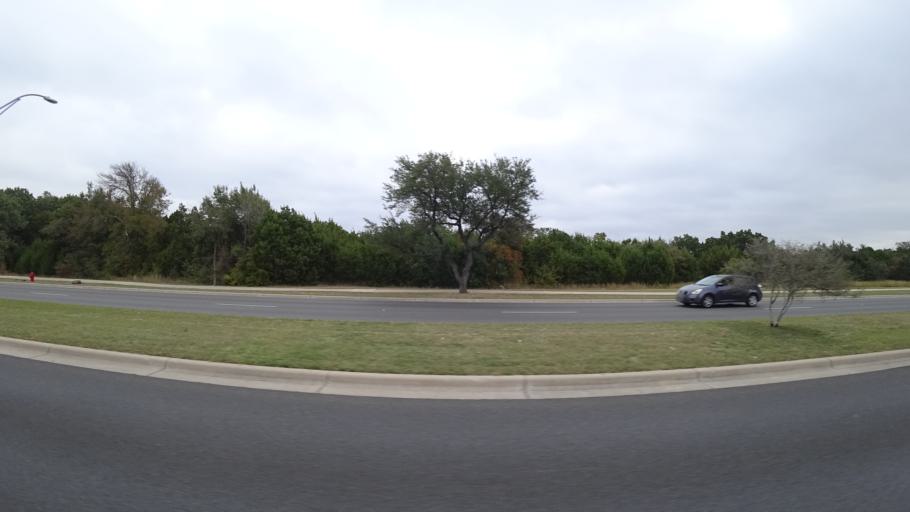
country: US
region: Texas
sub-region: Williamson County
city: Cedar Park
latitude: 30.5063
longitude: -97.8487
